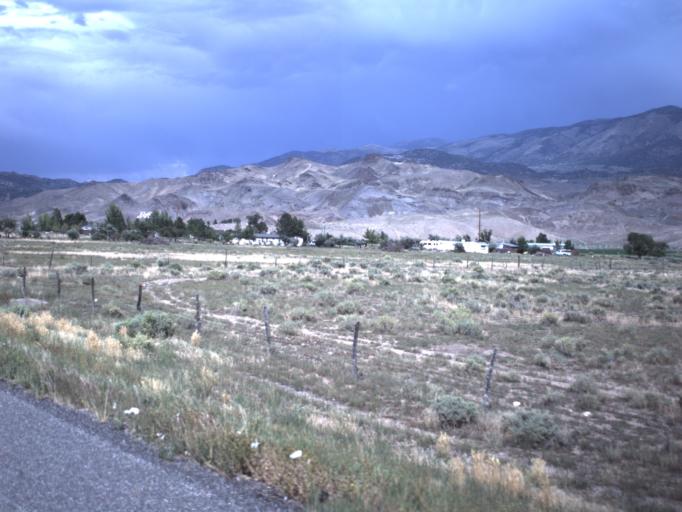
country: US
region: Utah
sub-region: Piute County
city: Junction
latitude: 38.4377
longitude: -112.2304
